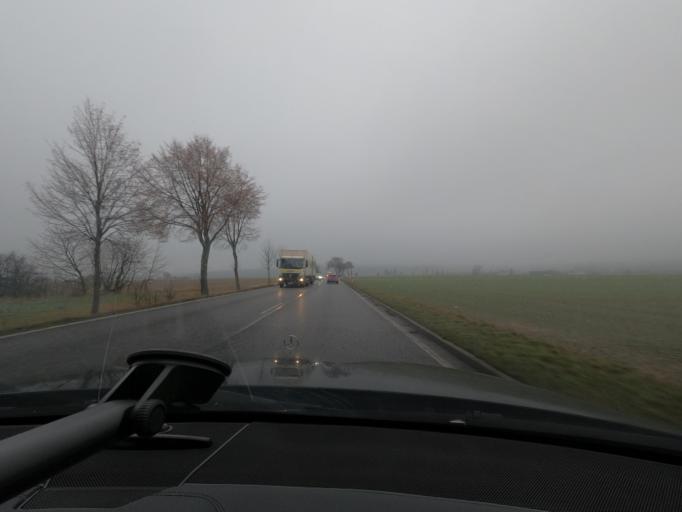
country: DE
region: Hesse
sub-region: Regierungsbezirk Kassel
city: Martinhagen
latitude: 51.3098
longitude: 9.2491
